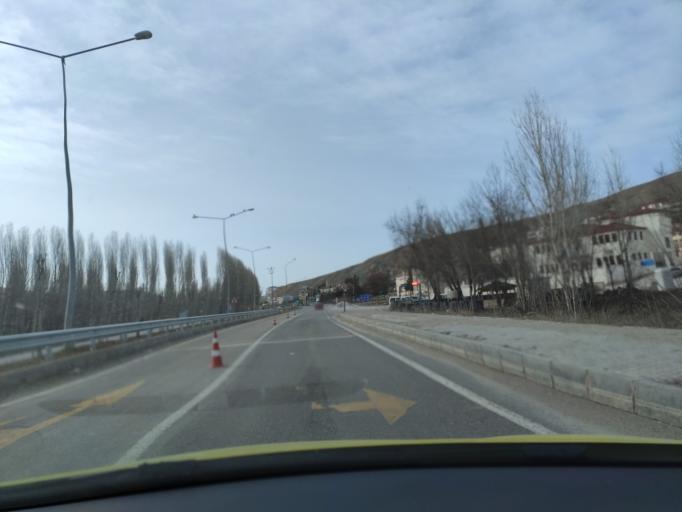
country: TR
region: Bayburt
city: Bayburt
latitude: 40.2402
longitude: 40.2482
